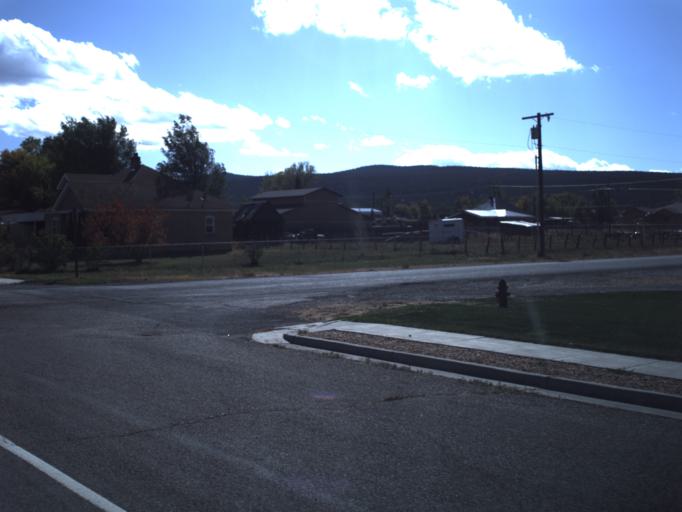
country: US
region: Utah
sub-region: Garfield County
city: Panguitch
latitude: 37.8184
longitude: -112.4356
